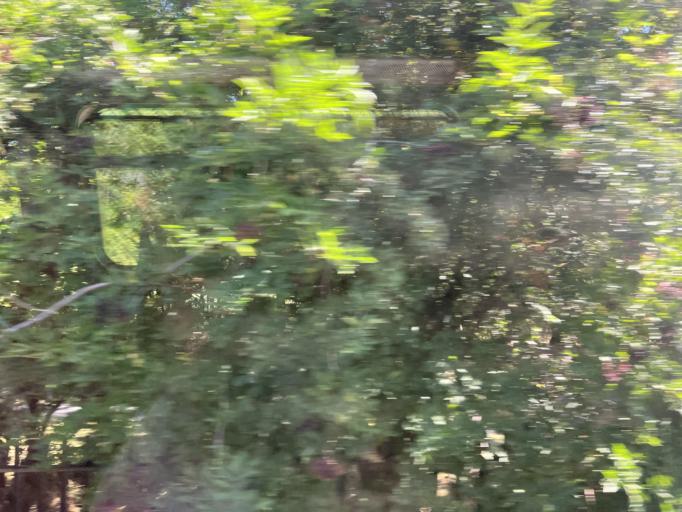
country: GB
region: England
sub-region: Lincolnshire
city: Spilsby
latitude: 53.0903
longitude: 0.0977
